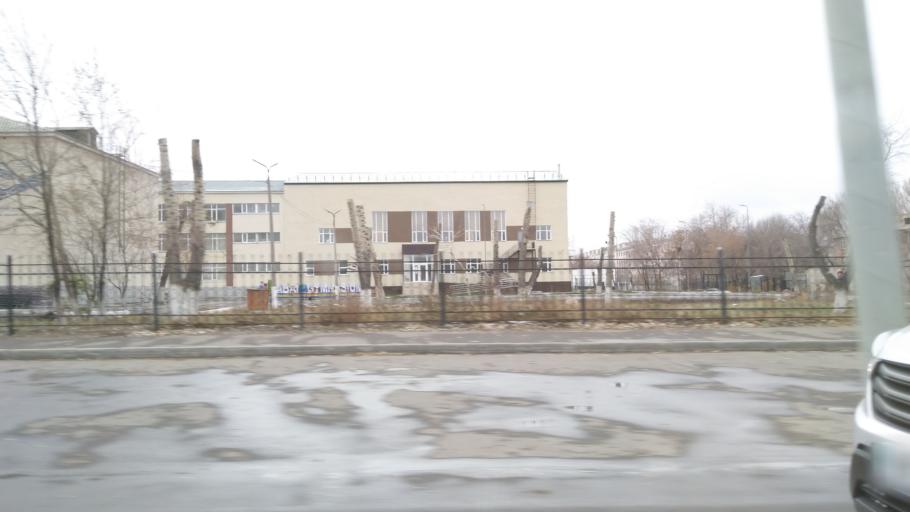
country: KZ
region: Pavlodar
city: Pavlodar
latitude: 52.2756
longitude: 76.9613
